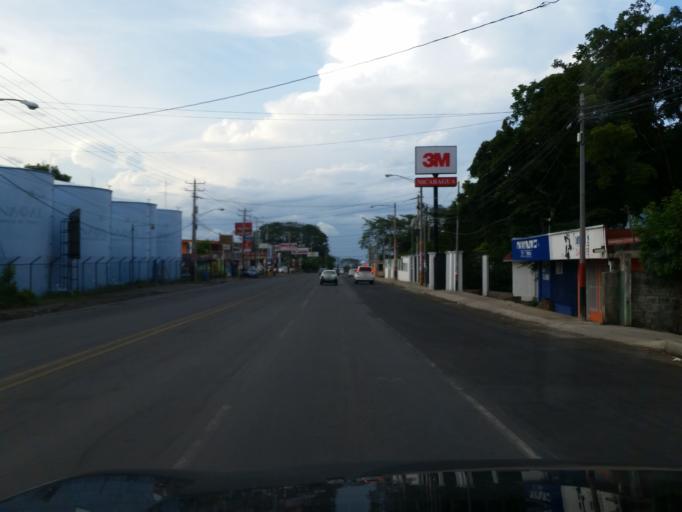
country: NI
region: Managua
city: Ciudad Sandino
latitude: 12.1122
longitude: -86.3158
